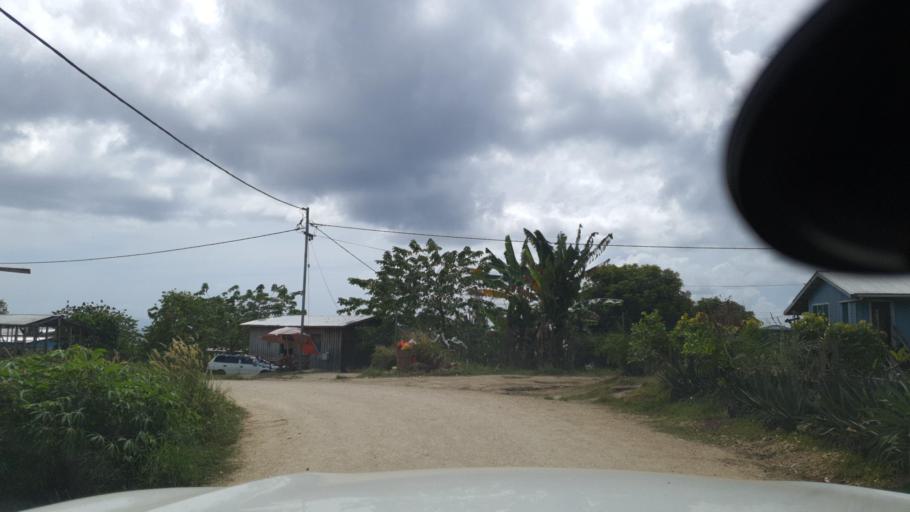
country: SB
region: Guadalcanal
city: Honiara
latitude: -9.4279
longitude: 159.9298
